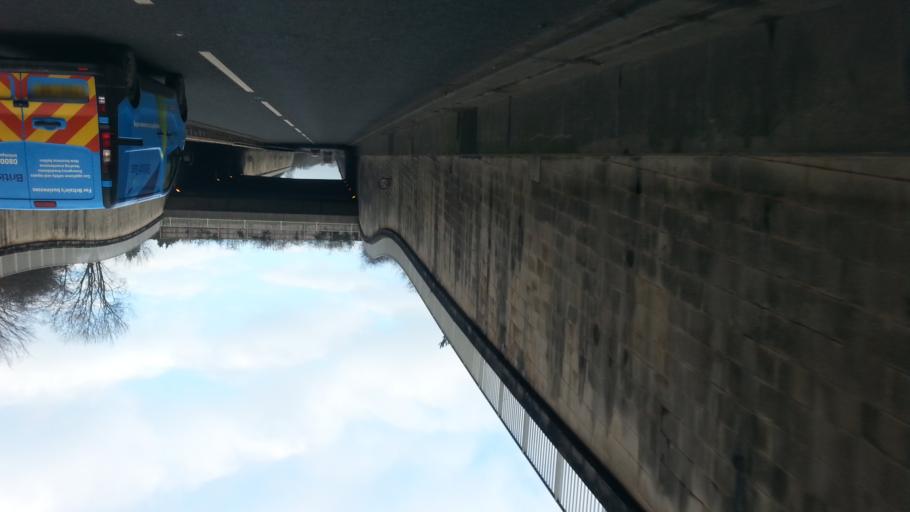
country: GB
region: England
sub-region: Bath and North East Somerset
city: Bath
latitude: 51.4018
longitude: -2.3385
